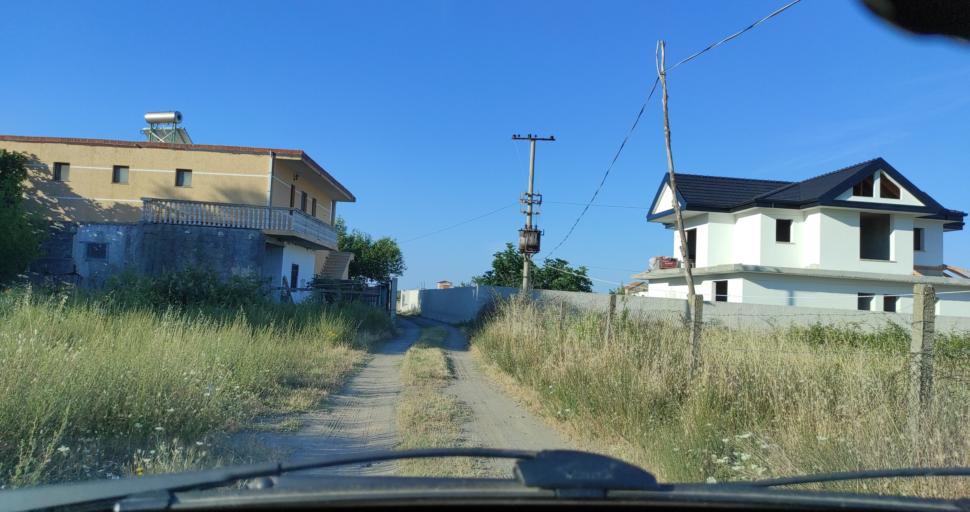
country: AL
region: Shkoder
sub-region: Rrethi i Shkodres
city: Velipoje
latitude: 41.8698
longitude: 19.4355
